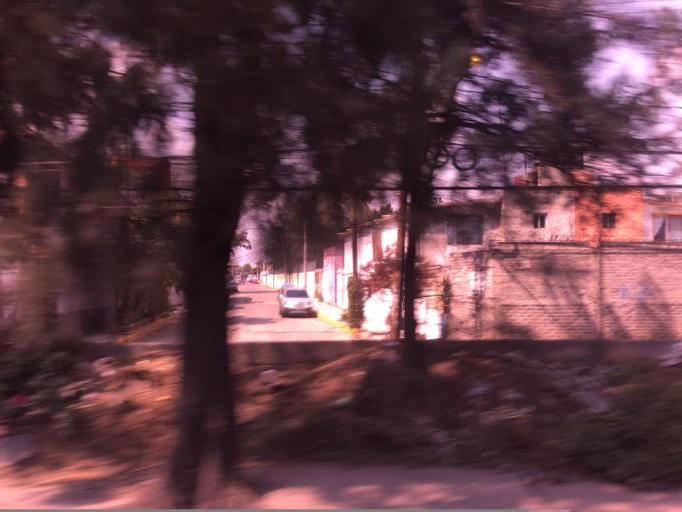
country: MX
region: Mexico
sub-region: Ciudad Nezahualcoyotl
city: Colonia Gustavo Baz Prada
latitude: 19.4554
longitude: -99.0437
